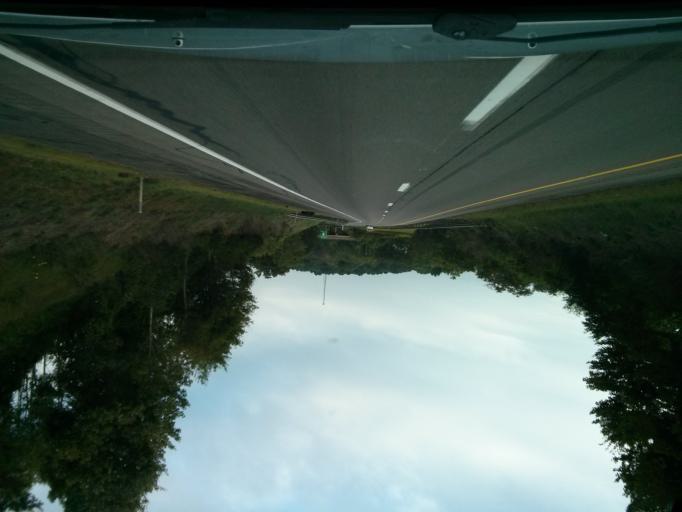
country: US
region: Pennsylvania
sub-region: Jefferson County
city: Brookville
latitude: 41.1686
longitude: -79.0692
